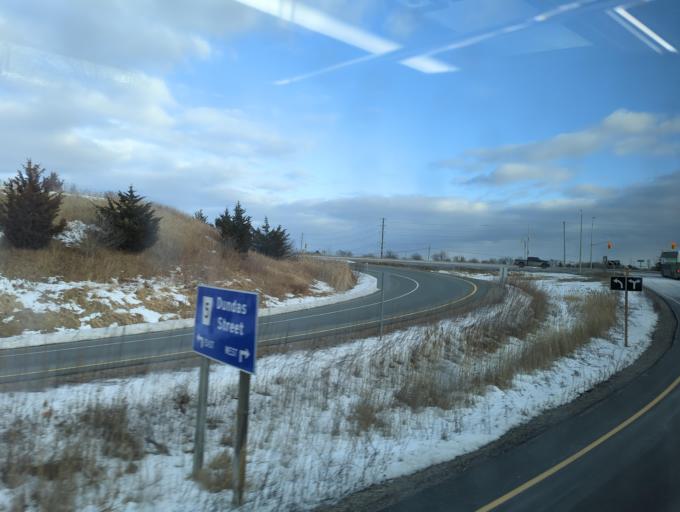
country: CA
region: Ontario
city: Burlington
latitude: 43.3831
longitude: -79.8359
